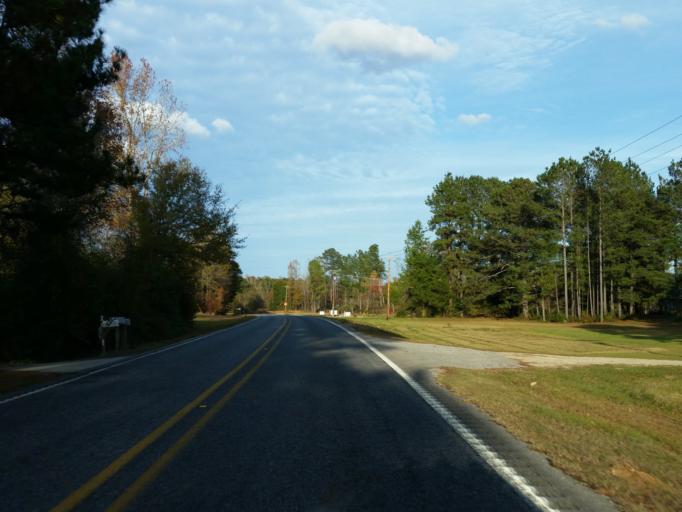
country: US
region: Mississippi
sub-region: Clarke County
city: Stonewall
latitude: 32.2195
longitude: -88.7767
